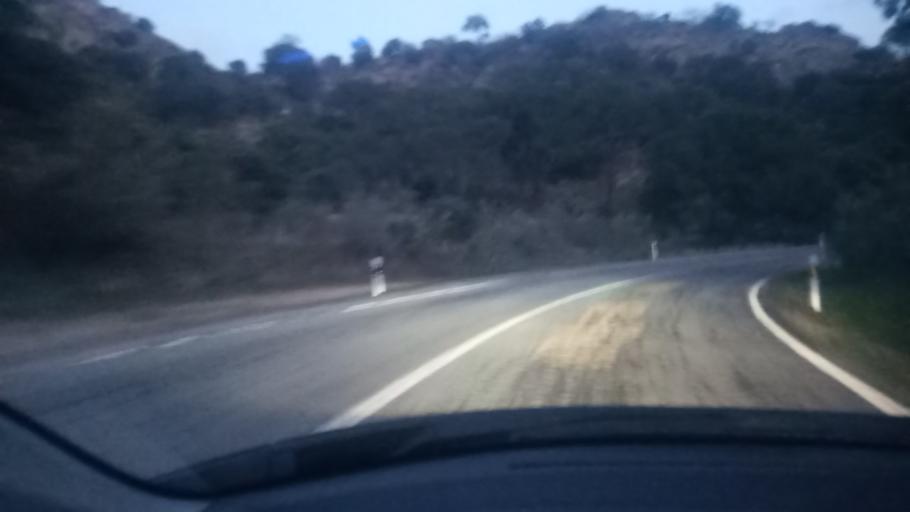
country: ES
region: Madrid
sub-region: Provincia de Madrid
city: Navas del Rey
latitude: 40.4341
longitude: -4.2618
